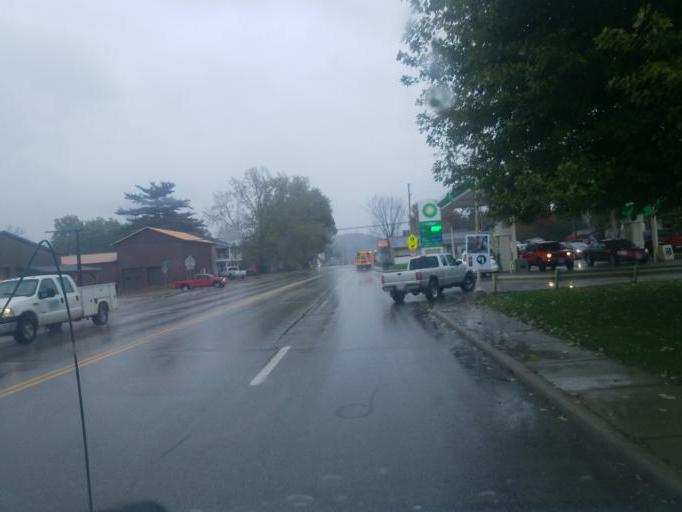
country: US
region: Ohio
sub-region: Muskingum County
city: Pleasant Grove
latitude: 39.8719
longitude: -81.9109
